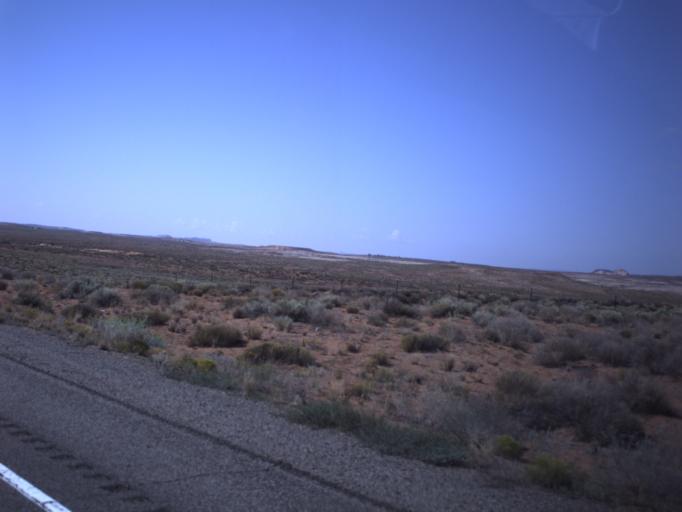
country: US
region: Utah
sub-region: San Juan County
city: Blanding
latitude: 37.2261
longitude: -109.6177
